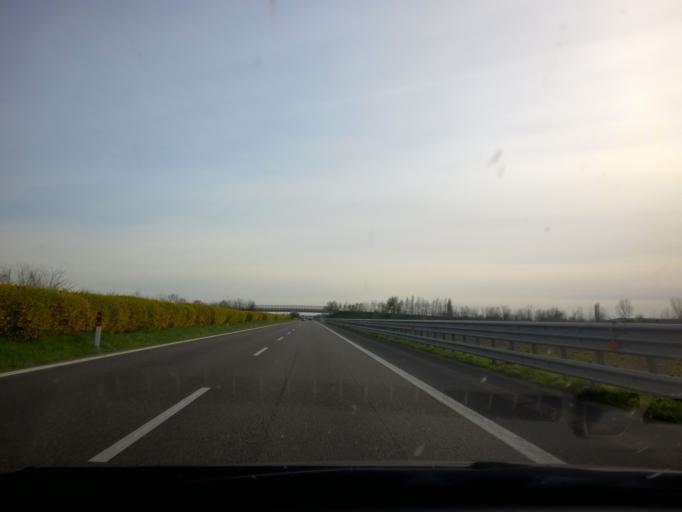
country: IT
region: Lombardy
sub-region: Provincia di Brescia
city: Manerbio
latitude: 45.3356
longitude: 10.1547
